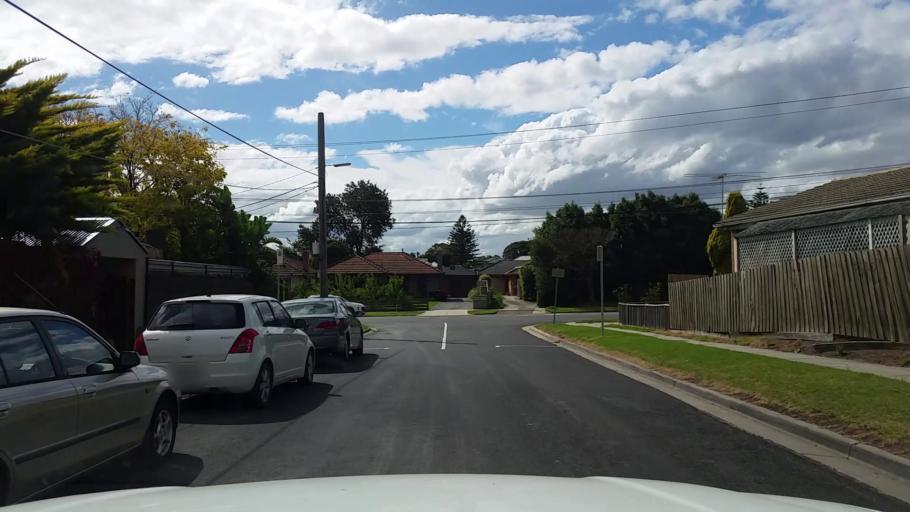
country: AU
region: Victoria
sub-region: Frankston
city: Frankston East
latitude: -38.1461
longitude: 145.1400
